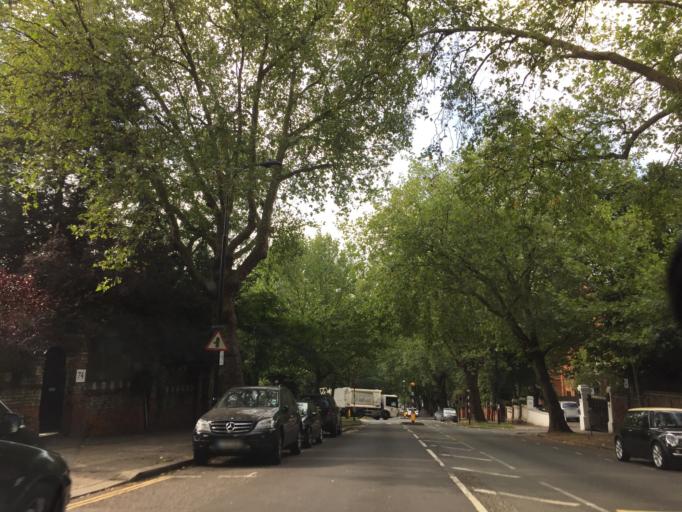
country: GB
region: England
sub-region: Greater London
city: Belsize Park
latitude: 51.5523
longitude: -0.1759
